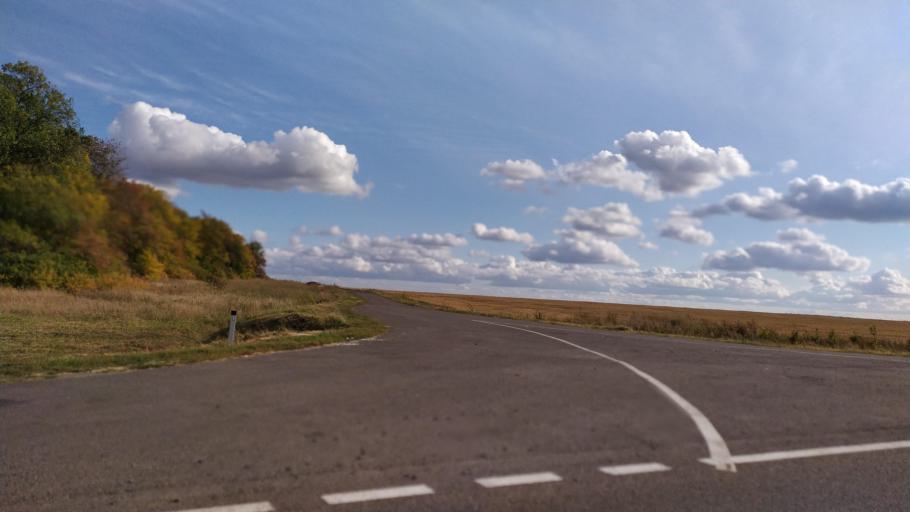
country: RU
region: Kursk
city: Kursk
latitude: 51.6147
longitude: 36.1642
